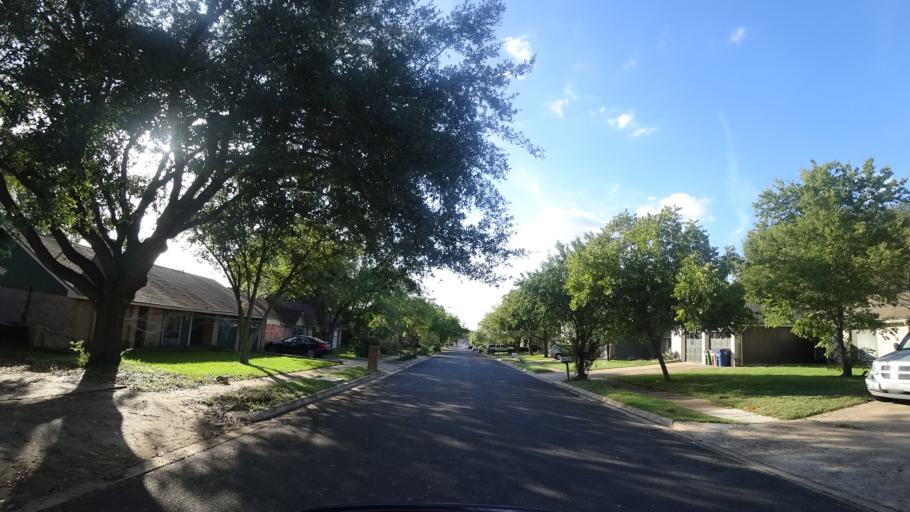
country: US
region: Texas
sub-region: Travis County
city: Onion Creek
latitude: 30.1979
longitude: -97.7961
